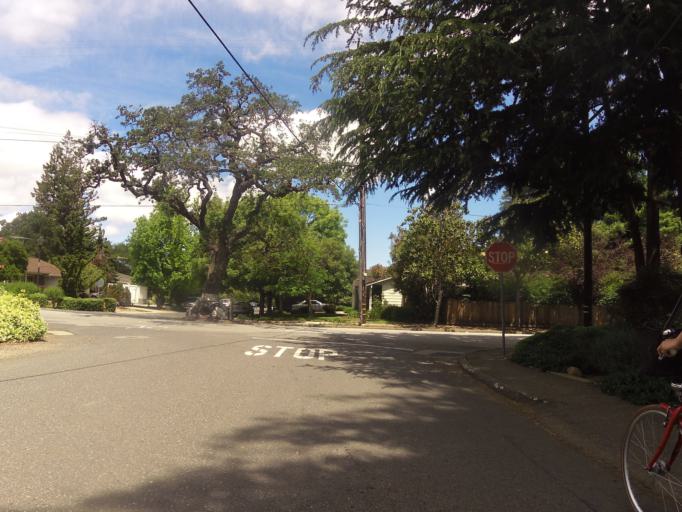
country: US
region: California
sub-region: Santa Clara County
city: Loyola
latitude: 37.3594
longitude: -122.0835
